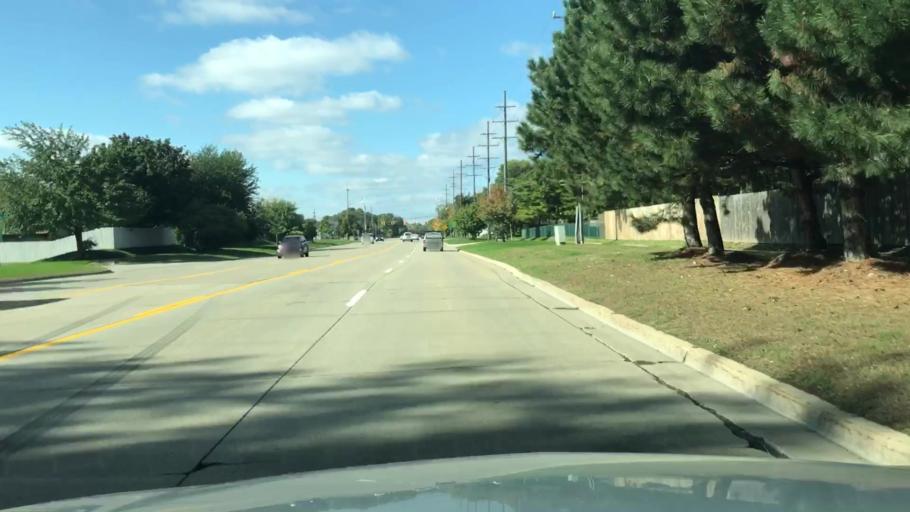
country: US
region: Michigan
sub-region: Macomb County
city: Sterling Heights
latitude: 42.5787
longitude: -83.0858
